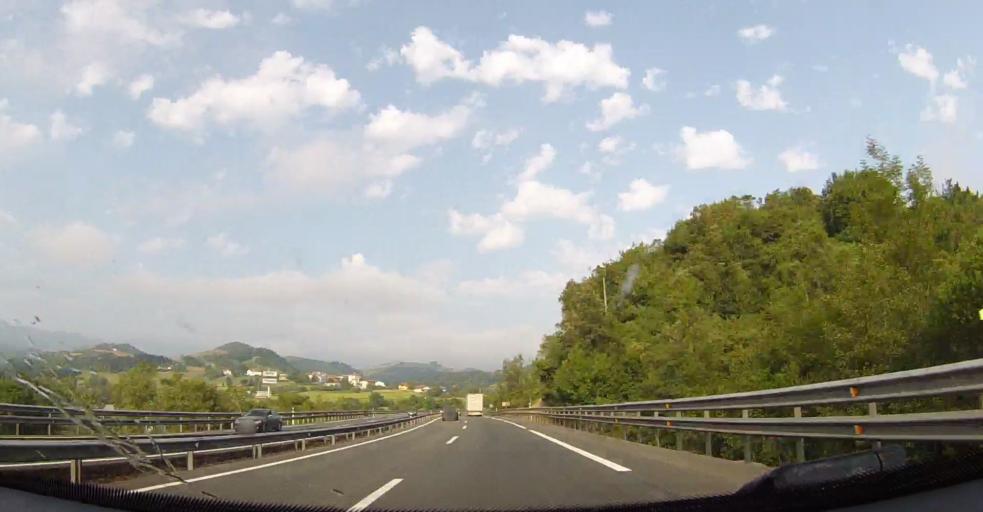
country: ES
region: Basque Country
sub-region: Provincia de Guipuzcoa
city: Getaria
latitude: 43.2854
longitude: -2.2226
